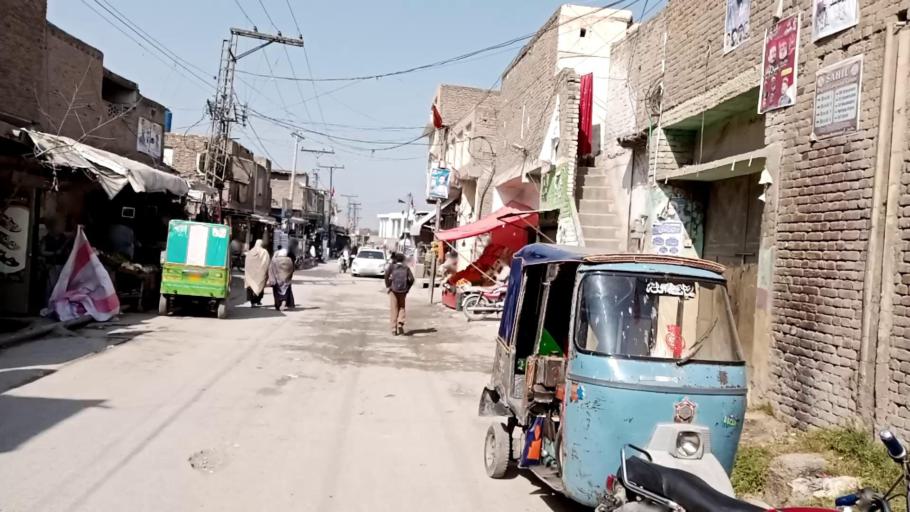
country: PK
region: Khyber Pakhtunkhwa
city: Peshawar
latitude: 34.0126
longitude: 71.5142
